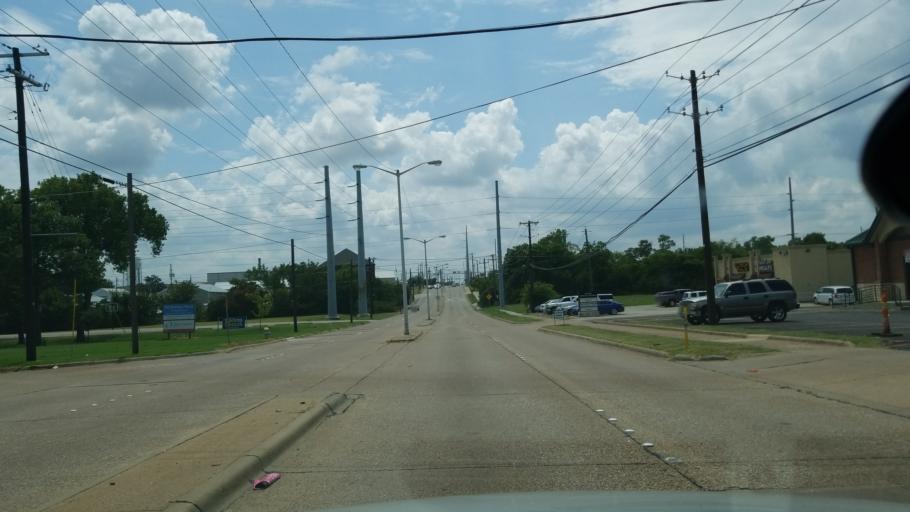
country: US
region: Texas
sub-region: Dallas County
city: Garland
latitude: 32.9152
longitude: -96.6653
